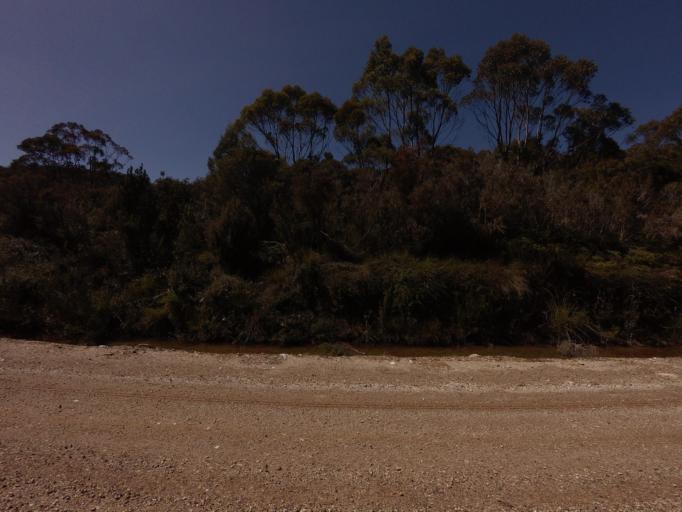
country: AU
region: Tasmania
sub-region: Huon Valley
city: Geeveston
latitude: -42.9933
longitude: 146.3716
